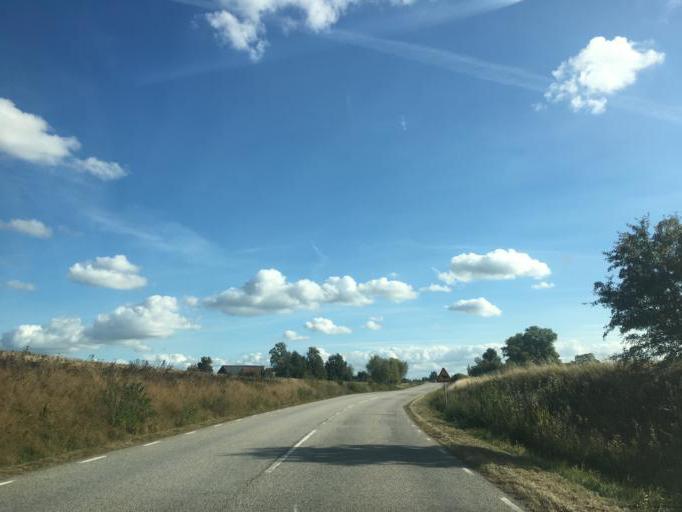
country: SE
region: Skane
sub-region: Svalovs Kommun
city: Teckomatorp
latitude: 55.8302
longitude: 13.0308
